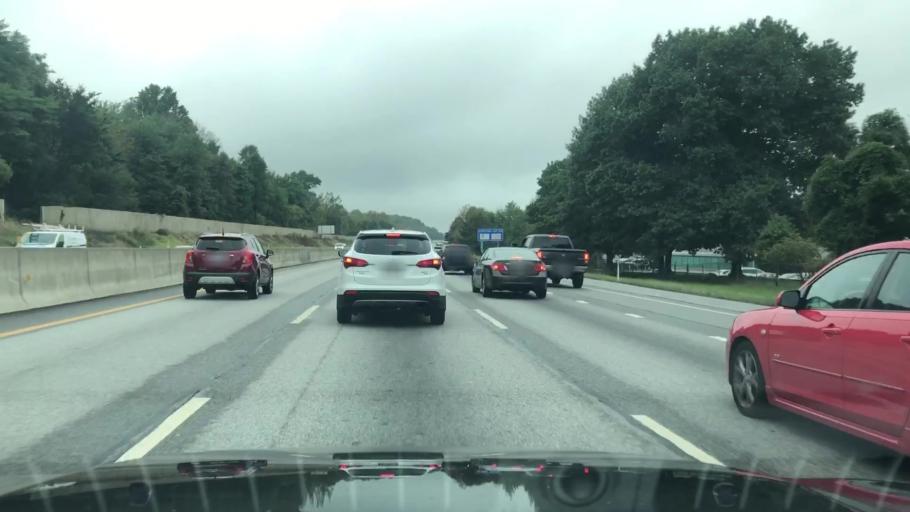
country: US
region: Pennsylvania
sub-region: Montgomery County
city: Dresher
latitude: 40.1354
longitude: -75.1772
